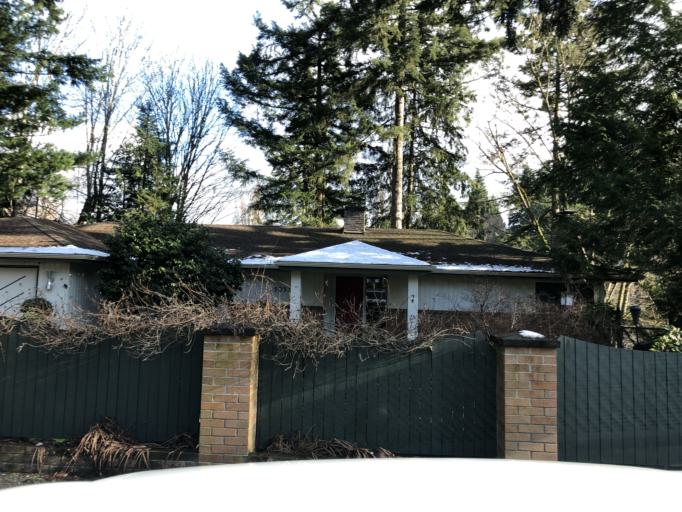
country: US
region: Washington
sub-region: King County
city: Shoreline
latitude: 47.7241
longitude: -122.3168
